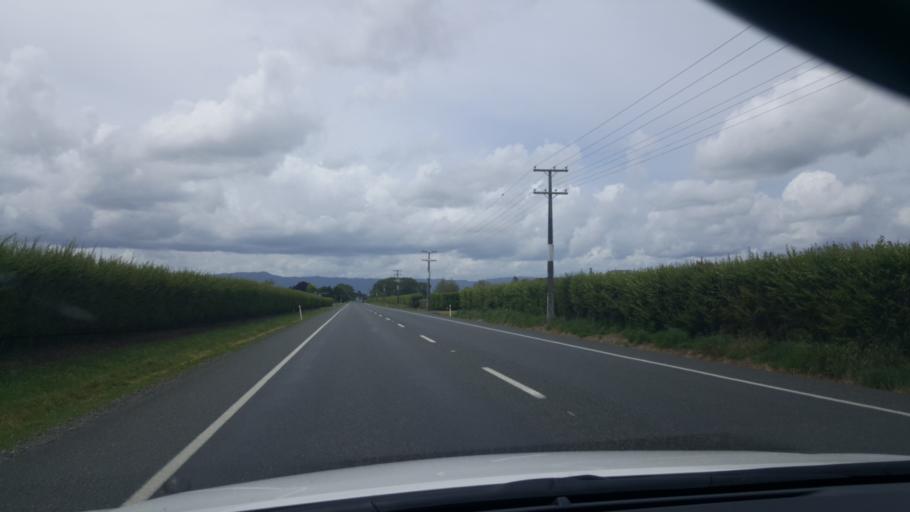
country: NZ
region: Waikato
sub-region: Matamata-Piako District
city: Matamata
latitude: -37.8823
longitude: 175.7384
